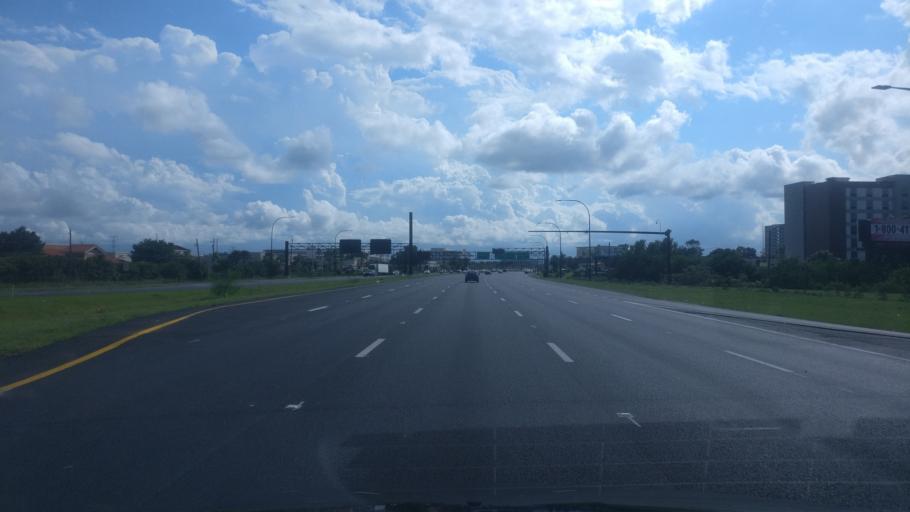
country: US
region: Florida
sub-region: Orange County
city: Tangelo Park
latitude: 28.4664
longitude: -81.4591
